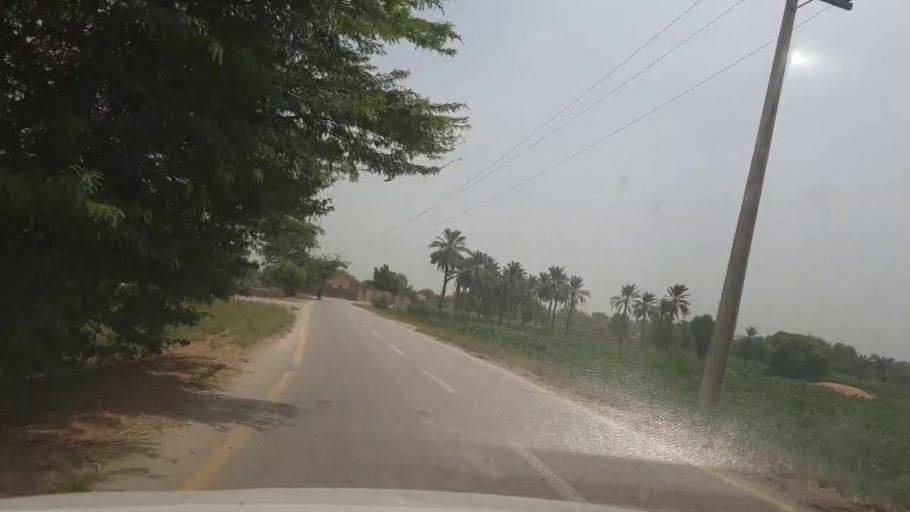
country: PK
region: Sindh
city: Kot Diji
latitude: 27.3691
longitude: 68.6454
